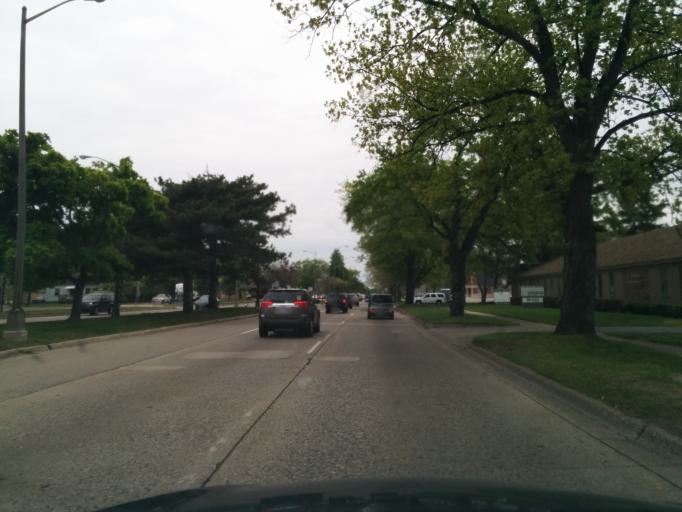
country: US
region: Michigan
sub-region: Ottawa County
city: Grand Haven
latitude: 43.0545
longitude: -86.2206
